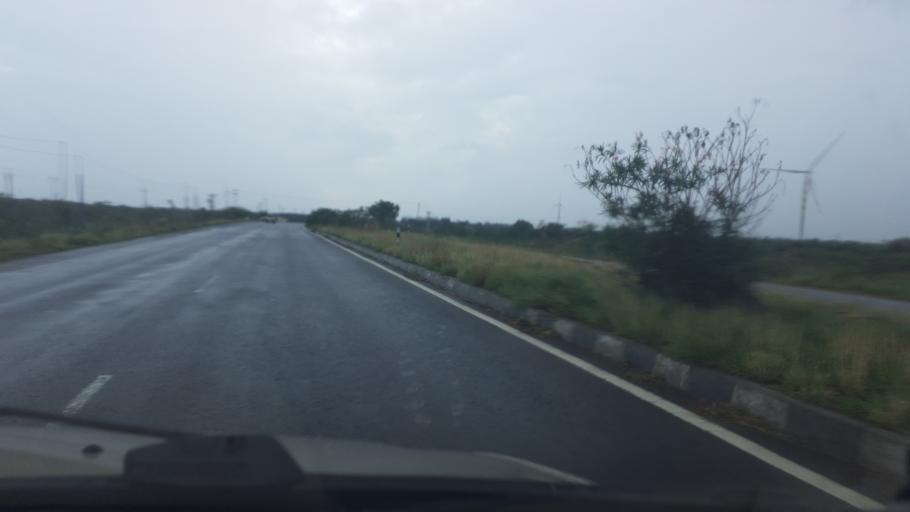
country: IN
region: Tamil Nadu
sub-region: Thoothukkudi
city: Kayattar
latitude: 8.9995
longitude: 77.7811
